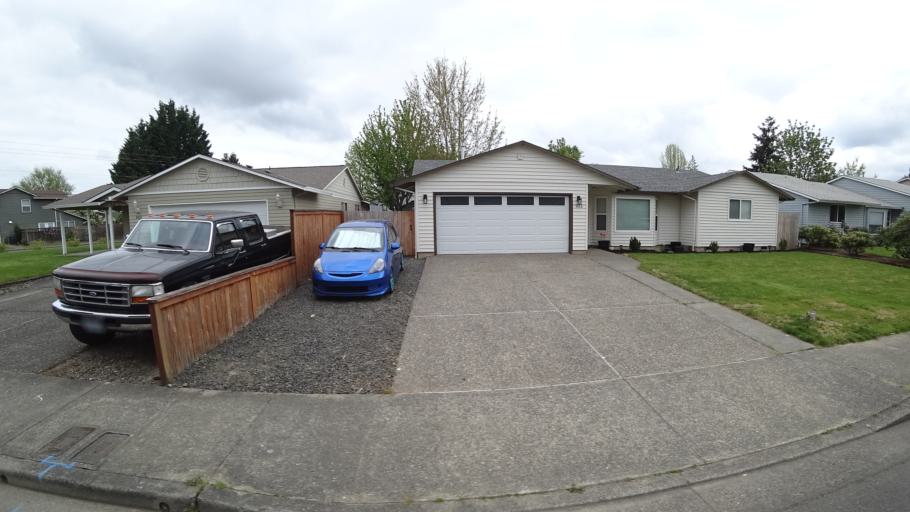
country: US
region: Oregon
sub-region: Washington County
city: Hillsboro
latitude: 45.5383
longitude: -122.9749
